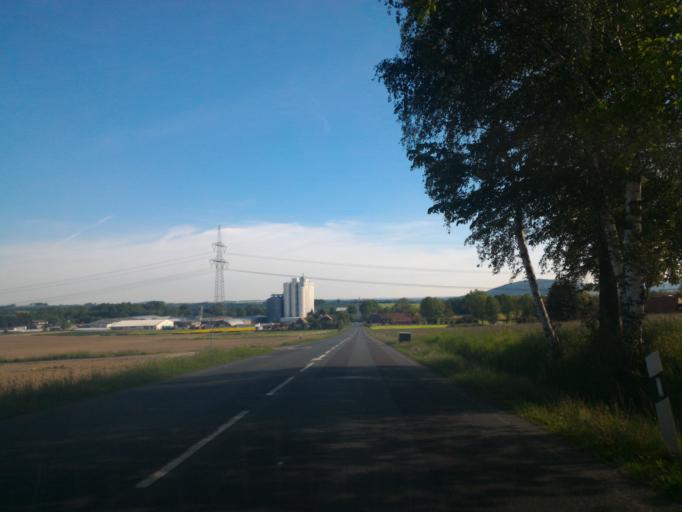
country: DE
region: Saxony
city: Durrhennersdorf
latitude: 51.0465
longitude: 14.6357
